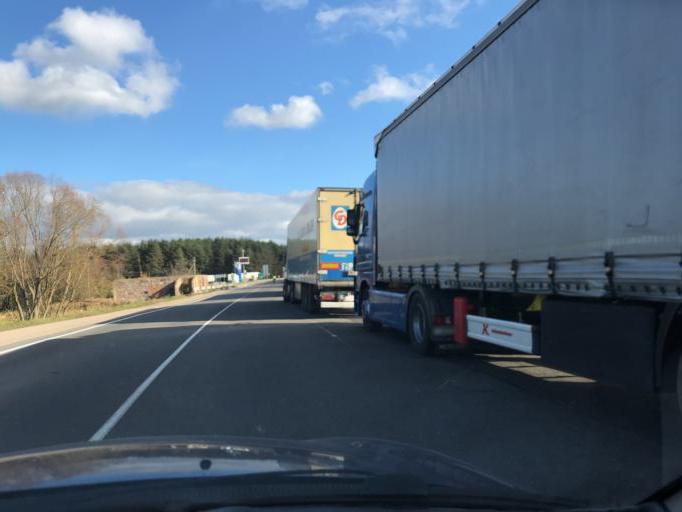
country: LT
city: Salcininkai
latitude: 54.2614
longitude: 25.3588
